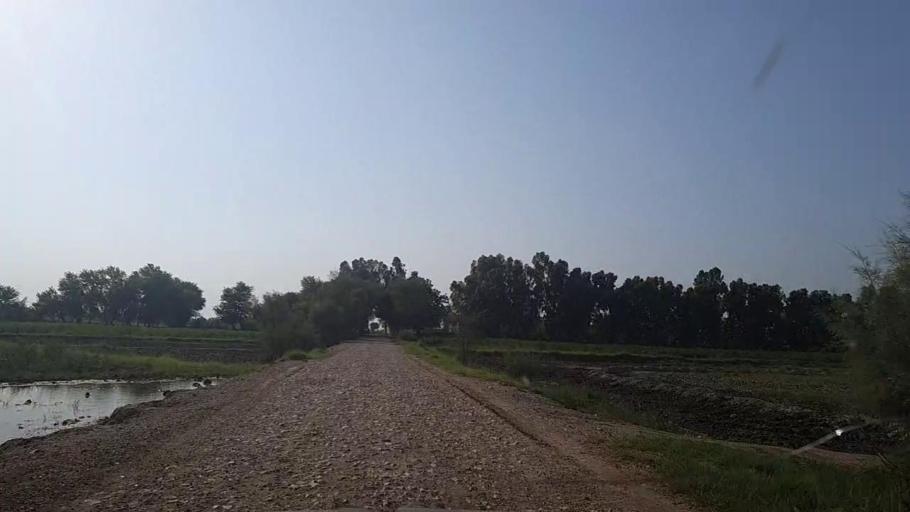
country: PK
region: Sindh
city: Khanpur
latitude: 27.7060
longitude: 69.3336
